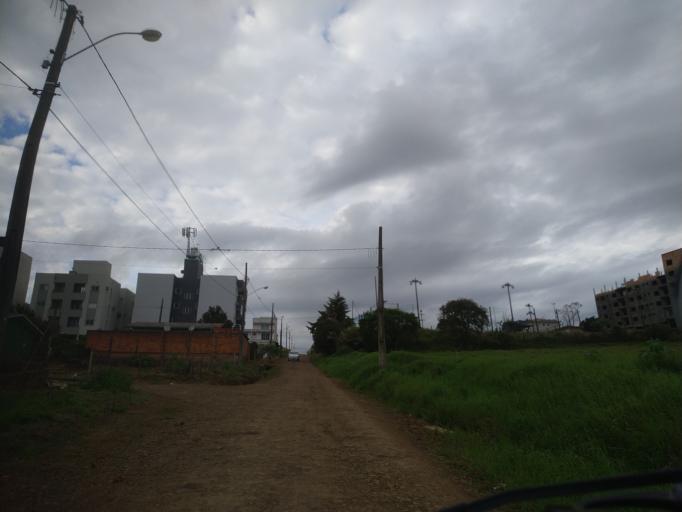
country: BR
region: Santa Catarina
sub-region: Chapeco
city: Chapeco
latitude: -27.0692
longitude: -52.6114
